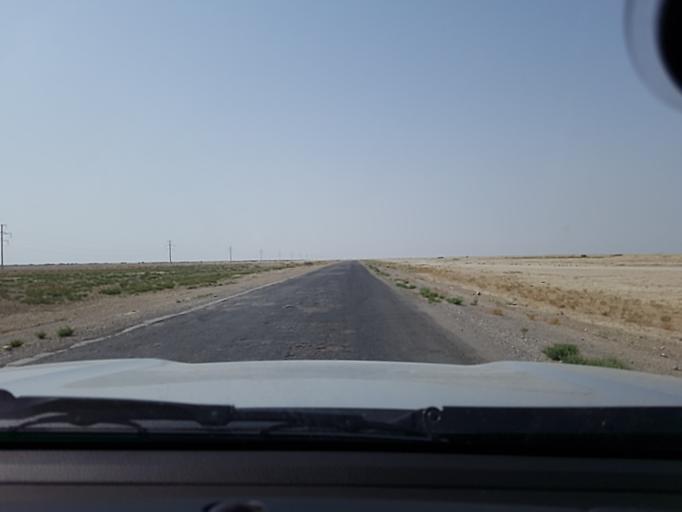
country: TM
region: Balkan
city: Gumdag
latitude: 38.8531
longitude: 54.5952
